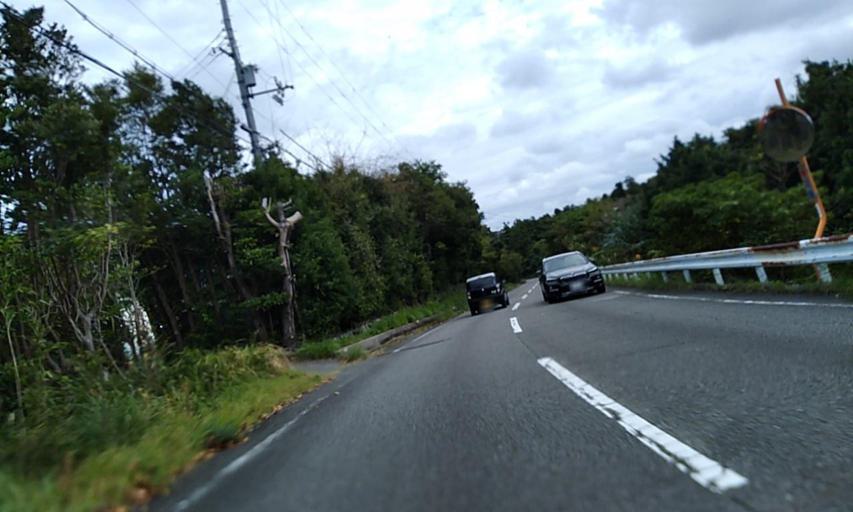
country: JP
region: Wakayama
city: Shingu
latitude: 33.4699
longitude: 135.8359
